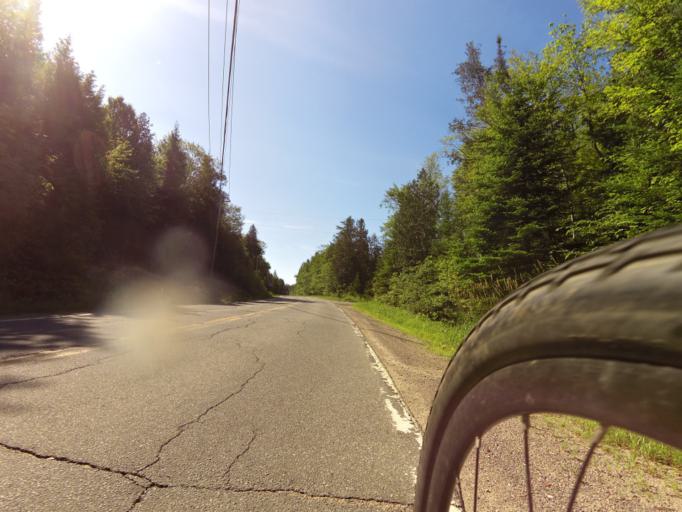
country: CA
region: Quebec
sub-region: Laurentides
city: Brownsburg-Chatham
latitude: 45.8374
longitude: -74.5646
